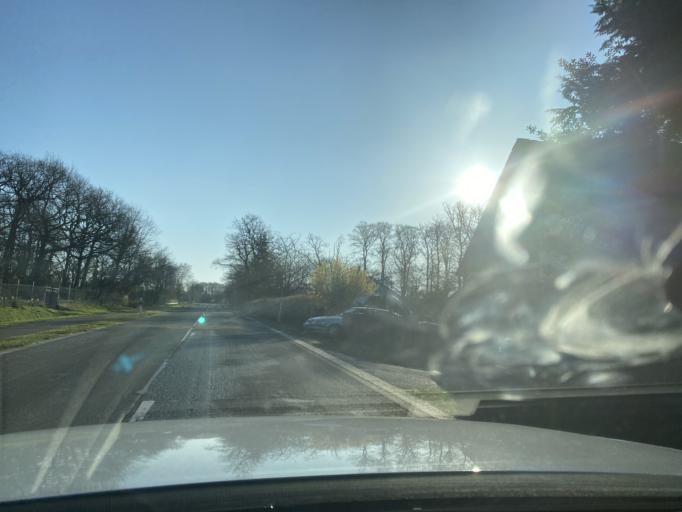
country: DE
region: North Rhine-Westphalia
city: Haan
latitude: 51.2284
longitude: 7.0267
